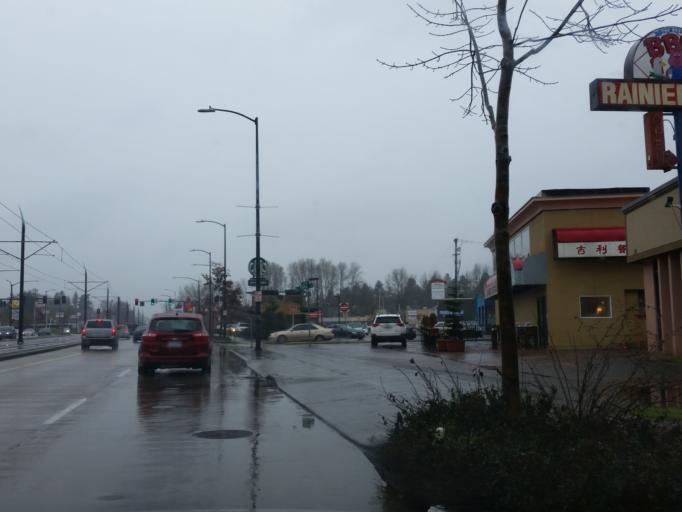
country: US
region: Washington
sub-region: King County
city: Riverton
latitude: 47.5449
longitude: -122.2849
